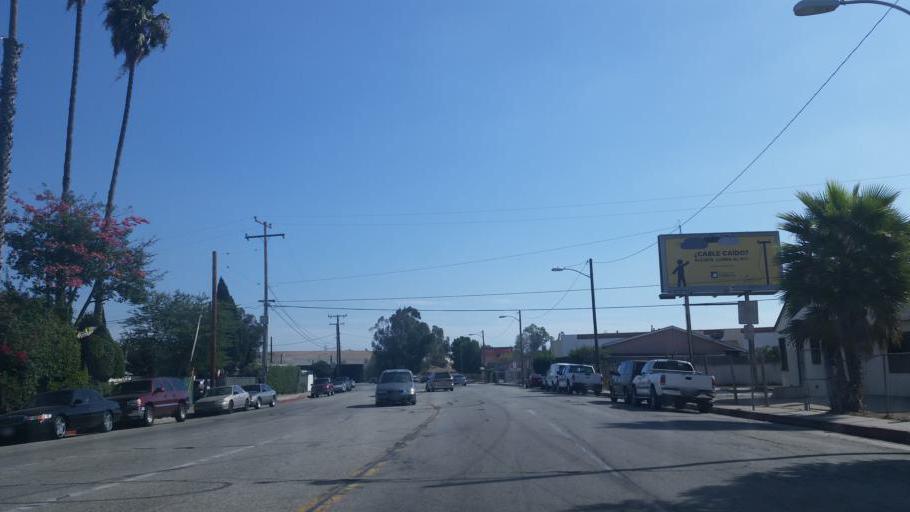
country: US
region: California
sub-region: Los Angeles County
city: East Rancho Dominguez
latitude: 33.8871
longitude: -118.1926
